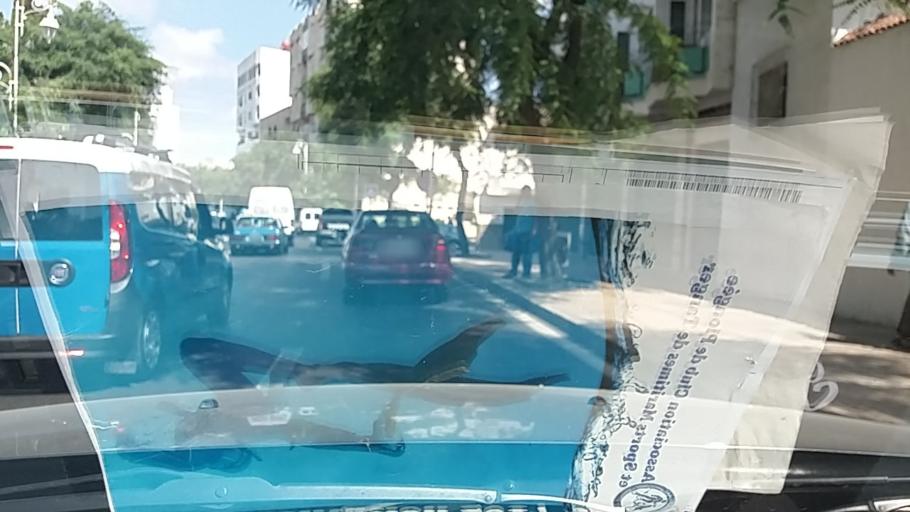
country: MA
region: Tanger-Tetouan
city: Tetouan
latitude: 35.5692
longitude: -5.3603
